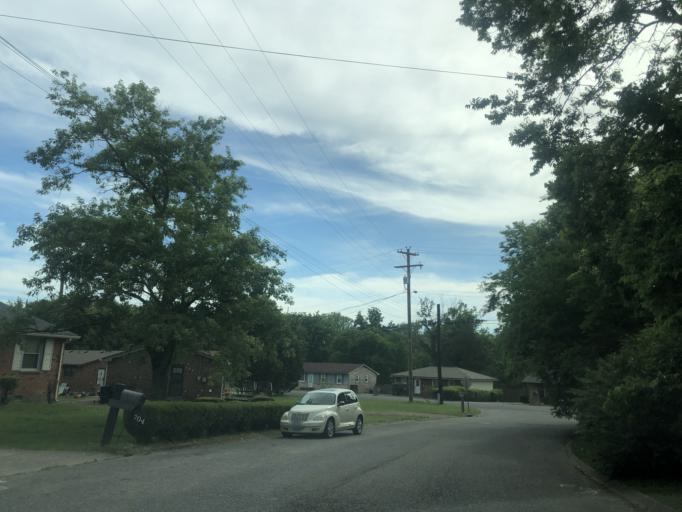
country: US
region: Tennessee
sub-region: Davidson County
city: Nashville
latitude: 36.2212
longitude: -86.8181
